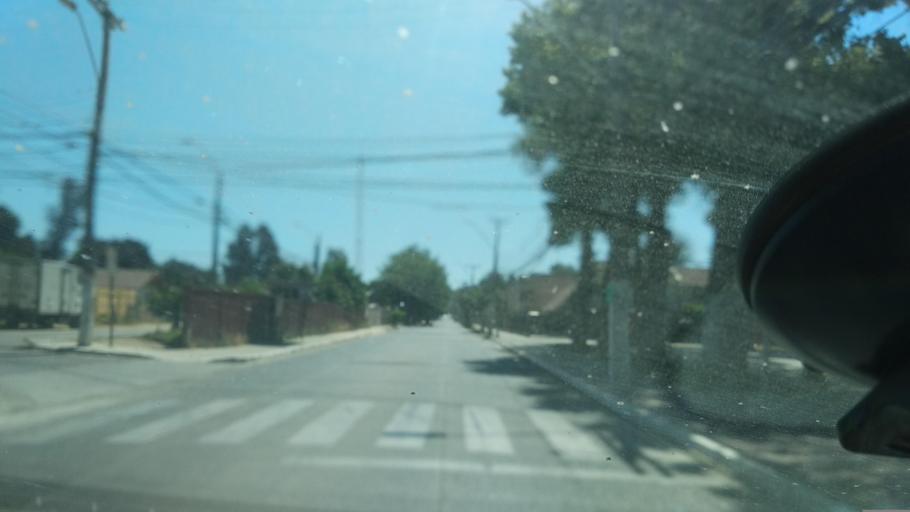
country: CL
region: Valparaiso
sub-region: Provincia de Marga Marga
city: Villa Alemana
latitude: -33.0460
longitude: -71.3576
